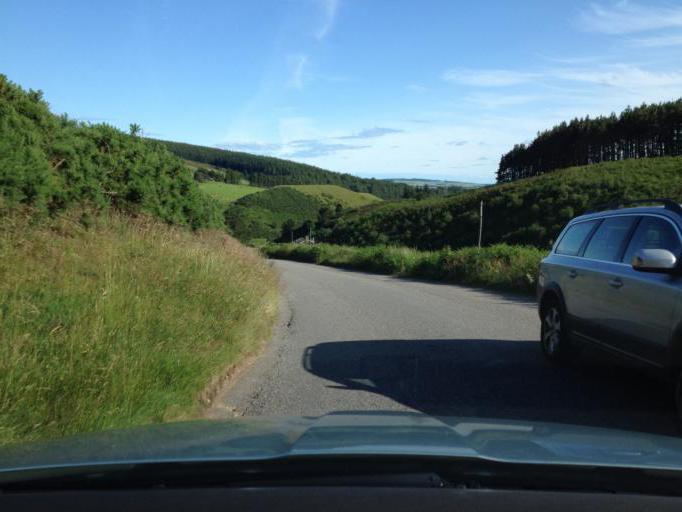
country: GB
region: Scotland
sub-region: Aberdeenshire
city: Laurencekirk
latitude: 56.8966
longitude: -2.5555
